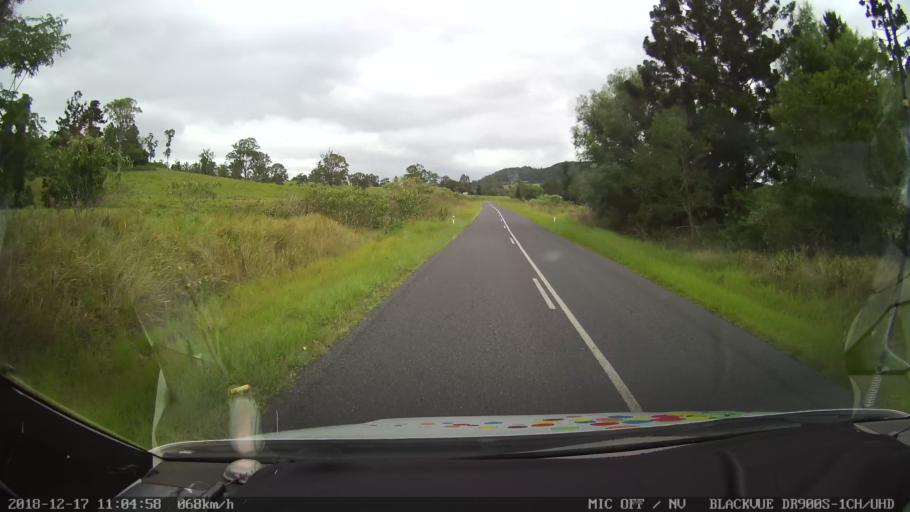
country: AU
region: New South Wales
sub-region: Kyogle
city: Kyogle
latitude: -28.7937
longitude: 152.6441
